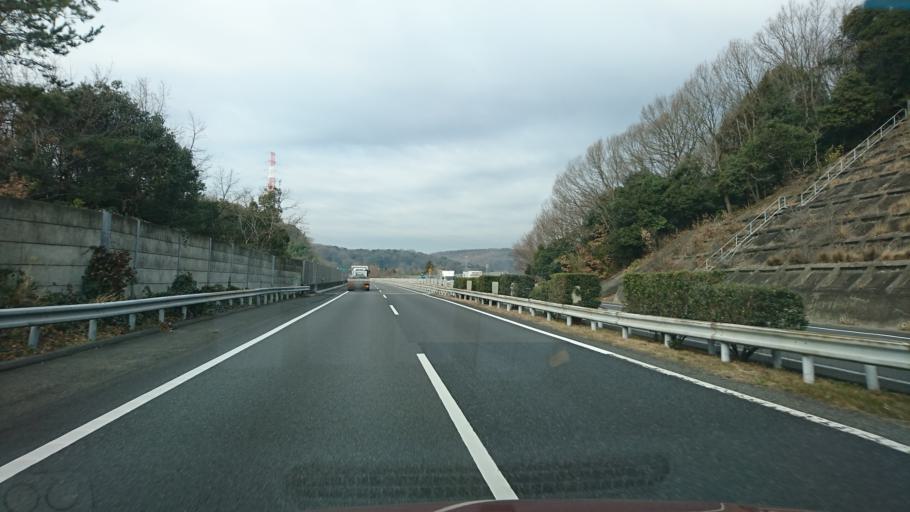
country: JP
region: Okayama
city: Kasaoka
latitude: 34.5339
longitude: 133.5244
